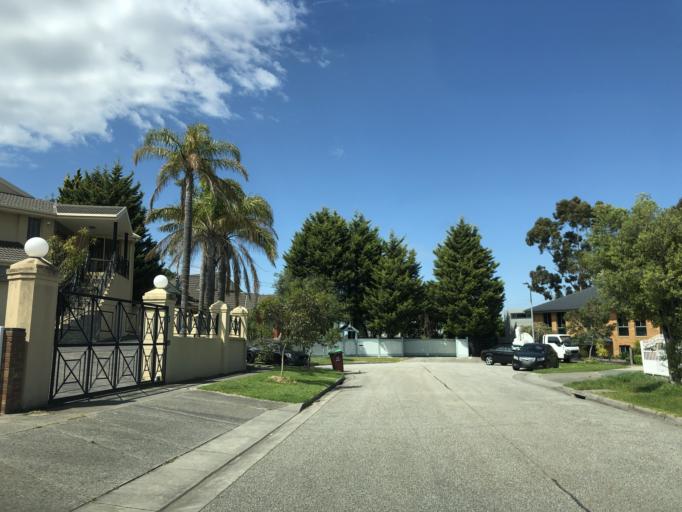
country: AU
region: Victoria
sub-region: Casey
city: Endeavour Hills
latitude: -37.9700
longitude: 145.2795
